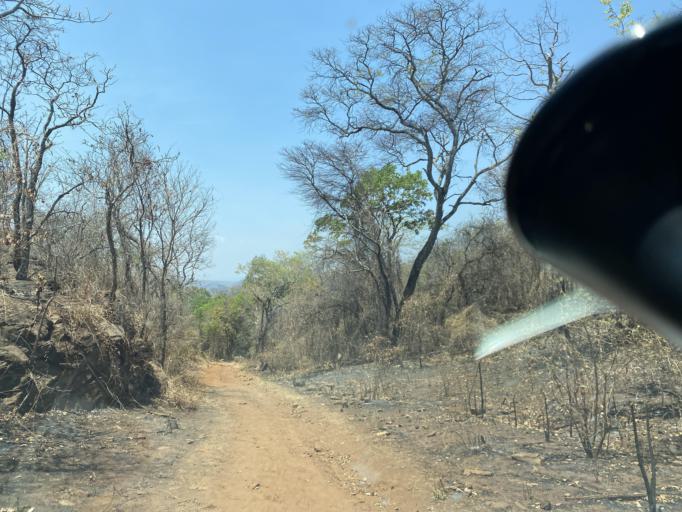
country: ZM
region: Lusaka
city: Kafue
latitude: -15.8037
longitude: 28.4485
